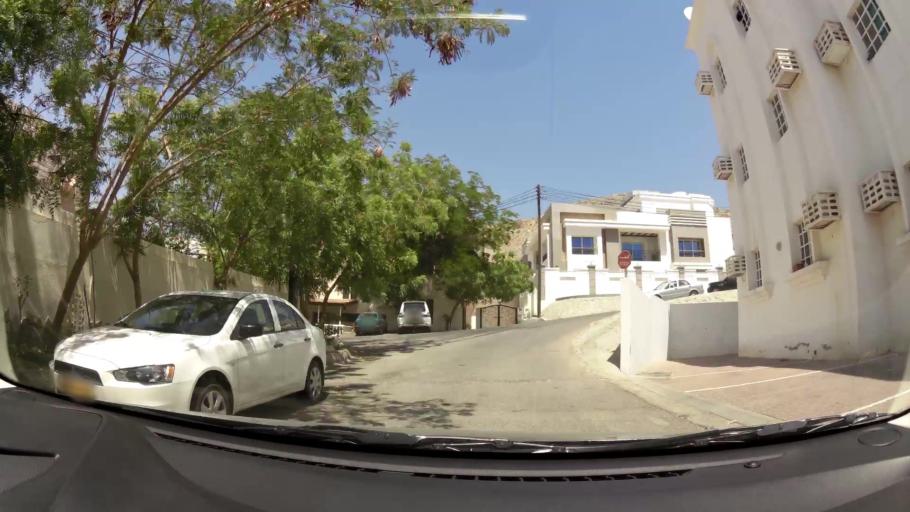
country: OM
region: Muhafazat Masqat
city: Muscat
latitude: 23.5971
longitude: 58.5349
